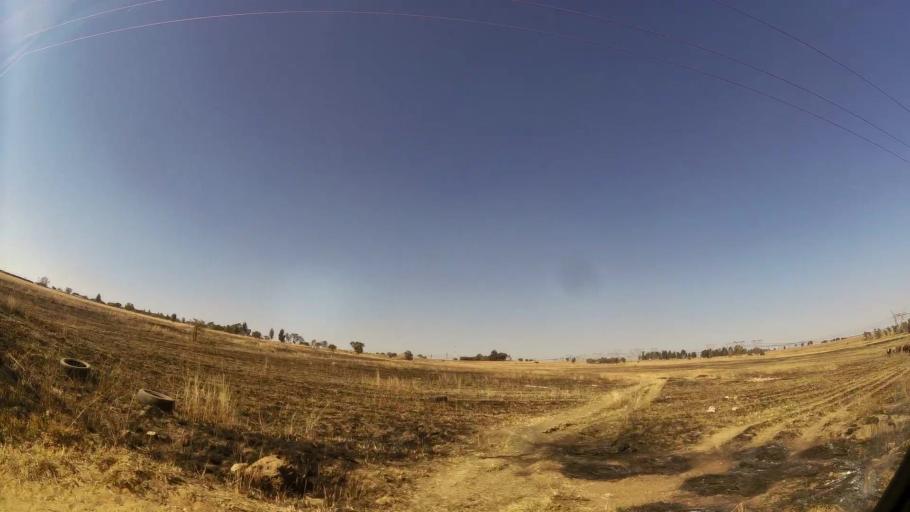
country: ZA
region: Gauteng
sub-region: City of Johannesburg Metropolitan Municipality
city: Diepsloot
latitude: -25.9051
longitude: 28.0721
